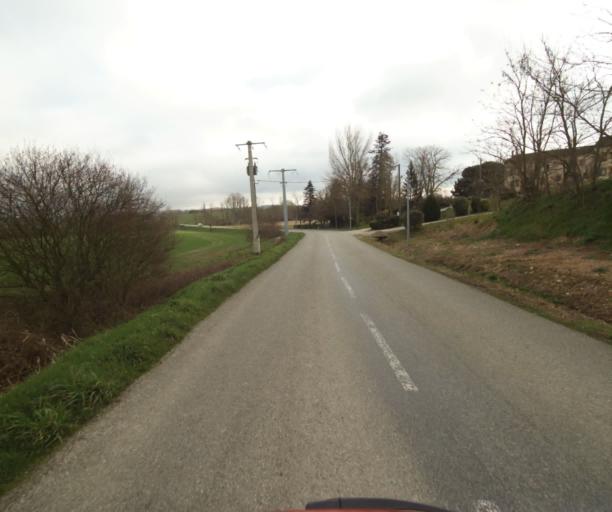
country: FR
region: Languedoc-Roussillon
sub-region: Departement de l'Aude
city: Belpech
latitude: 43.2123
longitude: 1.7255
